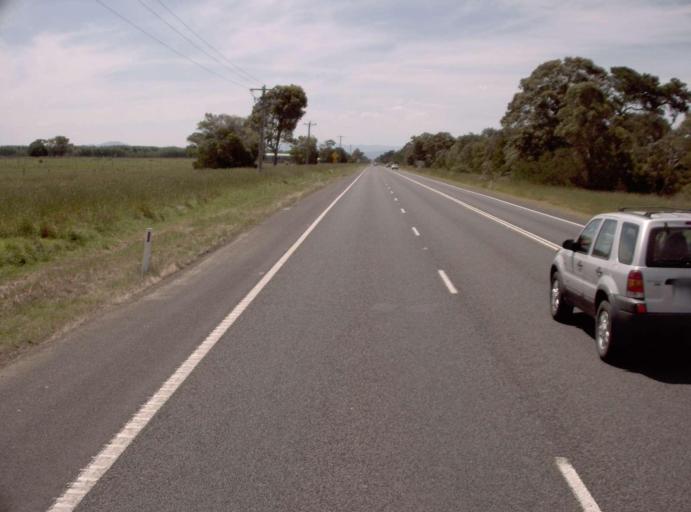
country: AU
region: Victoria
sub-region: Wellington
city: Sale
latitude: -38.0634
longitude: 147.0718
